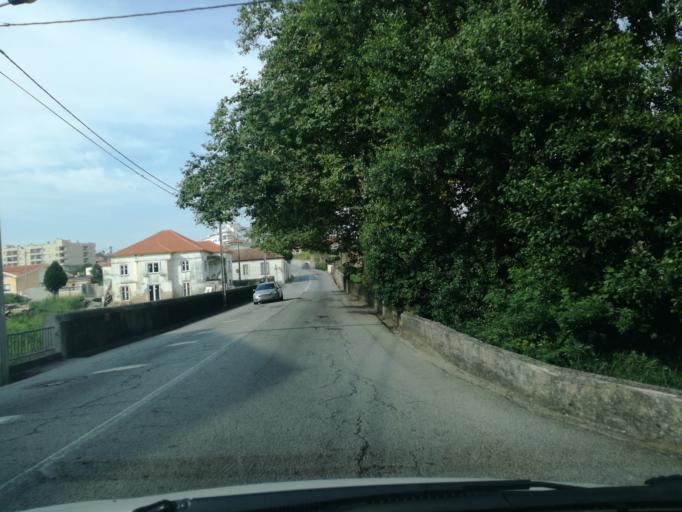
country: PT
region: Porto
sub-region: Vila Nova de Gaia
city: Sao Felix da Marinha
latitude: 41.0219
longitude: -8.6302
